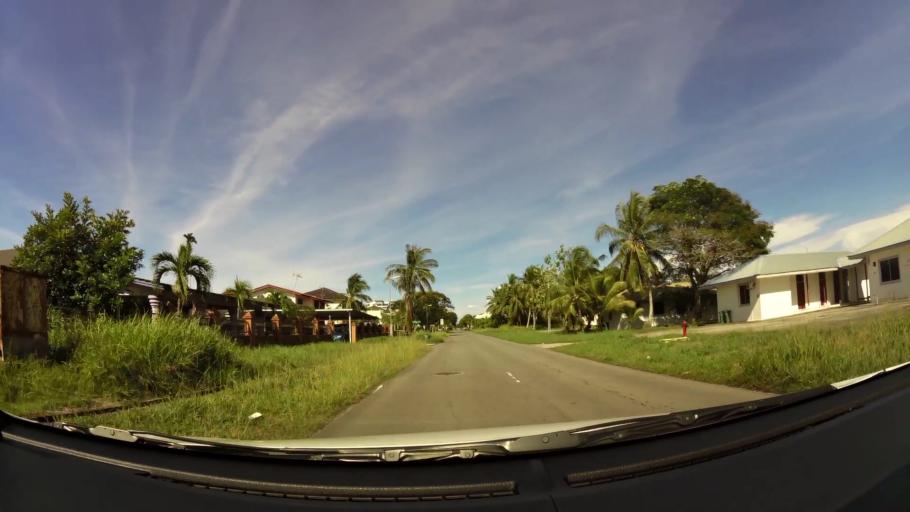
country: BN
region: Belait
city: Kuala Belait
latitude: 4.5828
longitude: 114.2062
